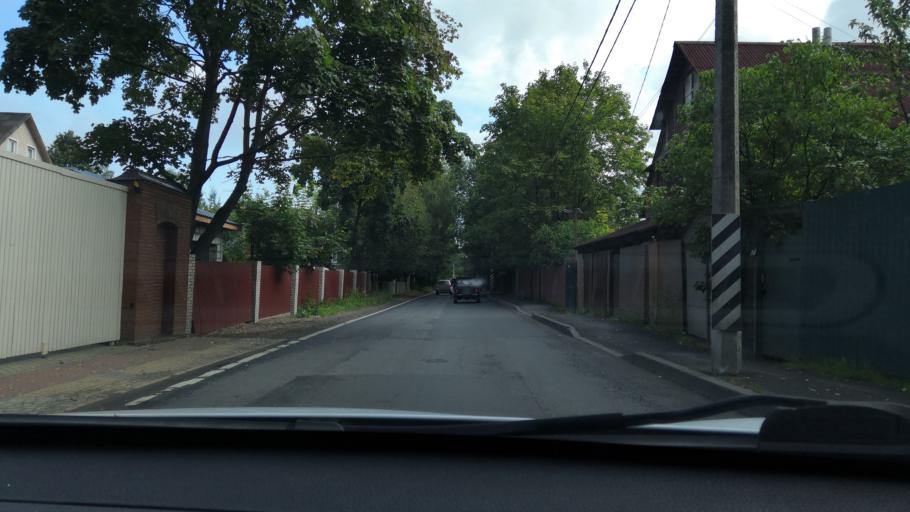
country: RU
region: St.-Petersburg
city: Pavlovsk
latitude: 59.6947
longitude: 30.4309
